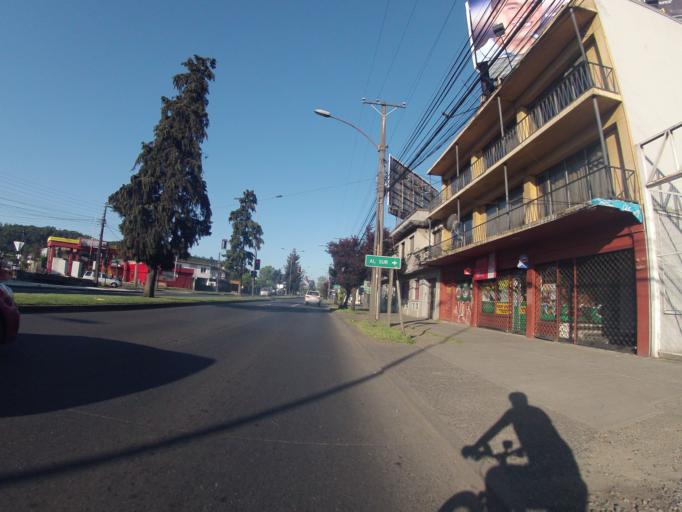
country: CL
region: Araucania
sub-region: Provincia de Cautin
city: Temuco
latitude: -38.7370
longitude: -72.5955
